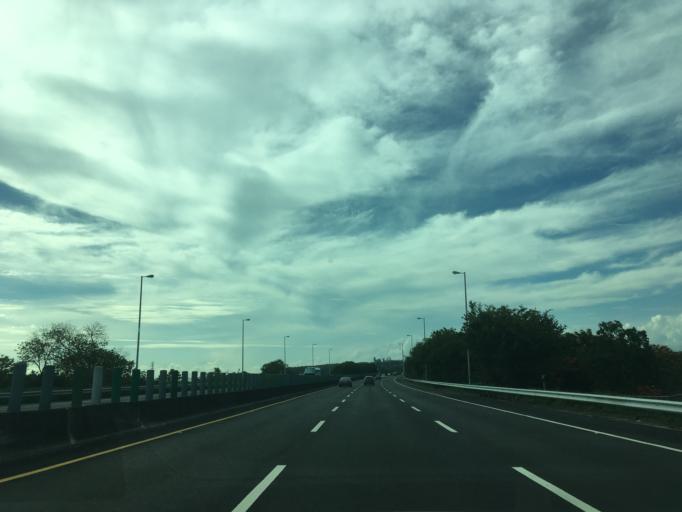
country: TW
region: Taiwan
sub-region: Chiayi
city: Jiayi Shi
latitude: 23.5073
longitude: 120.4888
